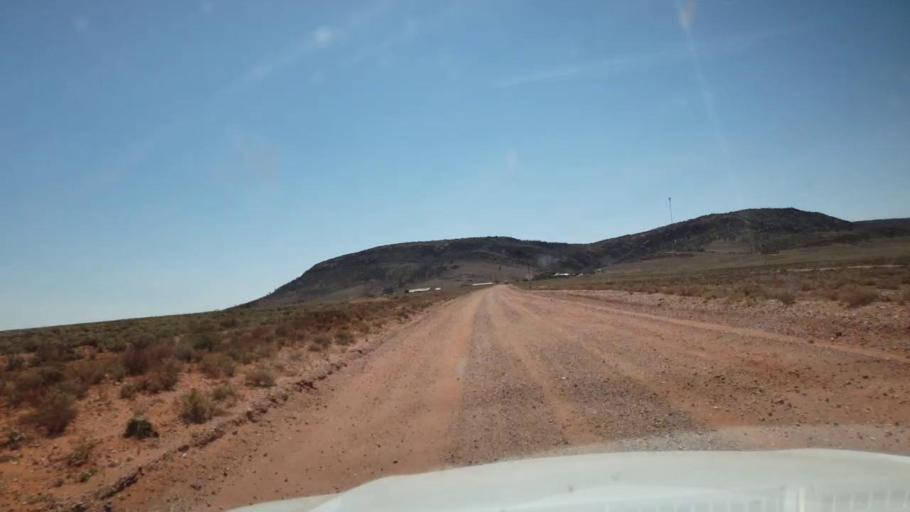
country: AU
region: South Australia
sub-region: Whyalla
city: Whyalla
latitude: -32.6924
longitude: 137.1294
